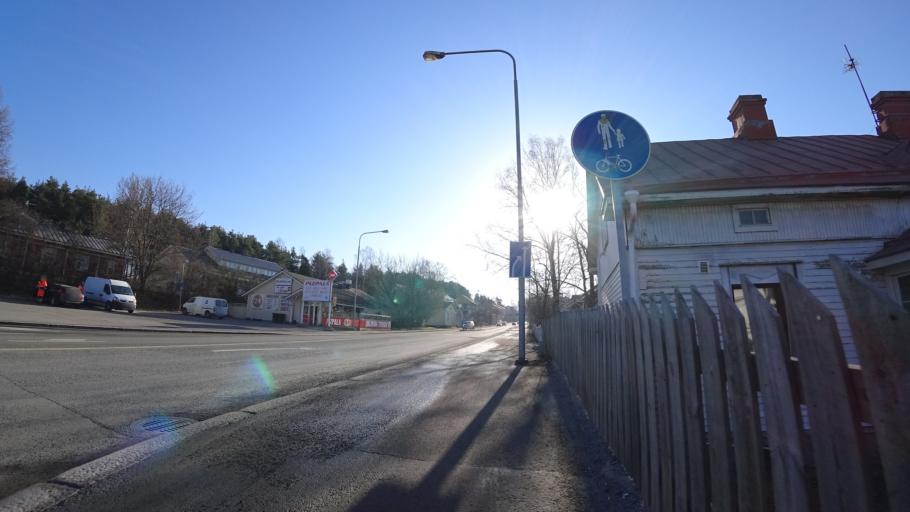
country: FI
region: Pirkanmaa
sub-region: Tampere
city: Pirkkala
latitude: 61.5061
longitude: 23.6998
